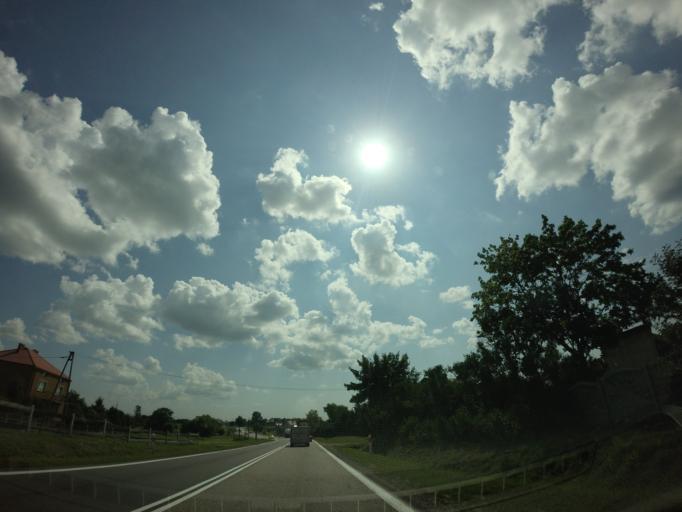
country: PL
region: Podlasie
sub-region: Powiat lomzynski
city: Piatnica
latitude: 53.2555
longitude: 22.1219
